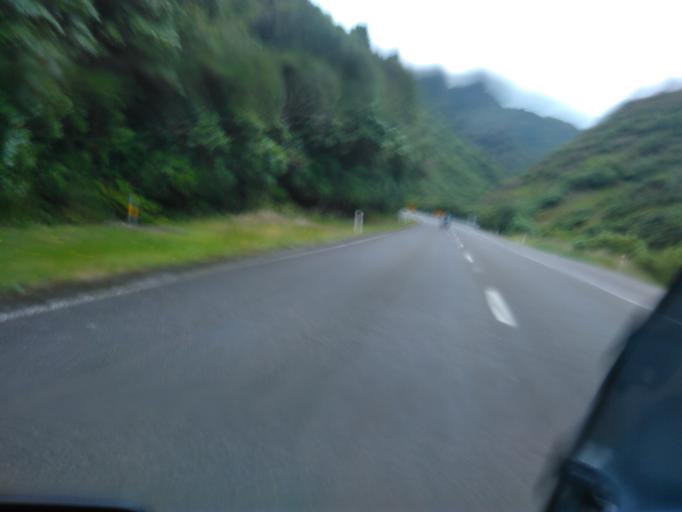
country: NZ
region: Bay of Plenty
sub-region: Opotiki District
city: Opotiki
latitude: -38.3377
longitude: 177.4214
